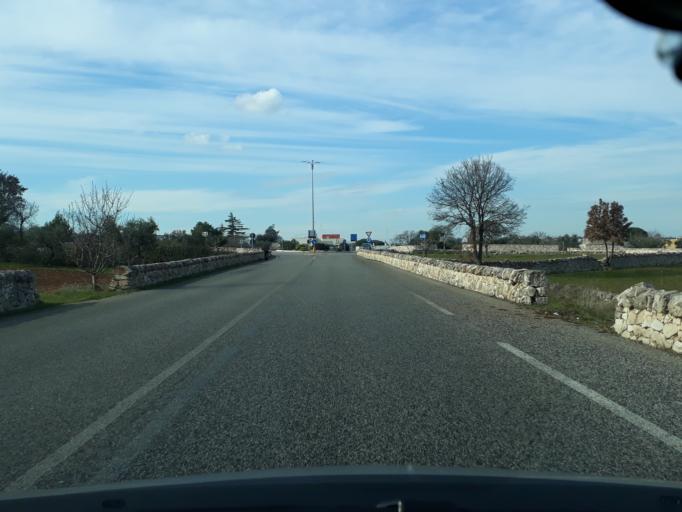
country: IT
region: Apulia
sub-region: Provincia di Bari
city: Locorotondo
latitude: 40.7611
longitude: 17.3341
